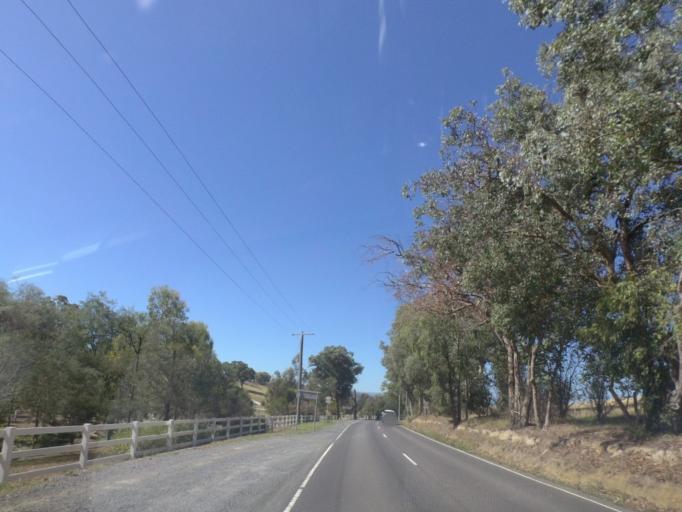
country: AU
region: Victoria
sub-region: Yarra Ranges
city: Chirnside Park
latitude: -37.7323
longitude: 145.2838
